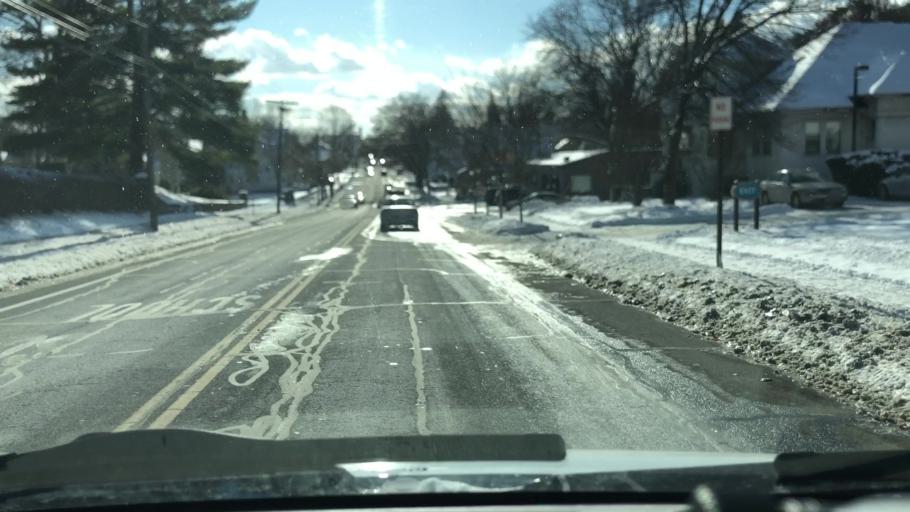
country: US
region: Massachusetts
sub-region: Franklin County
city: Greenfield
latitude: 42.5950
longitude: -72.5976
